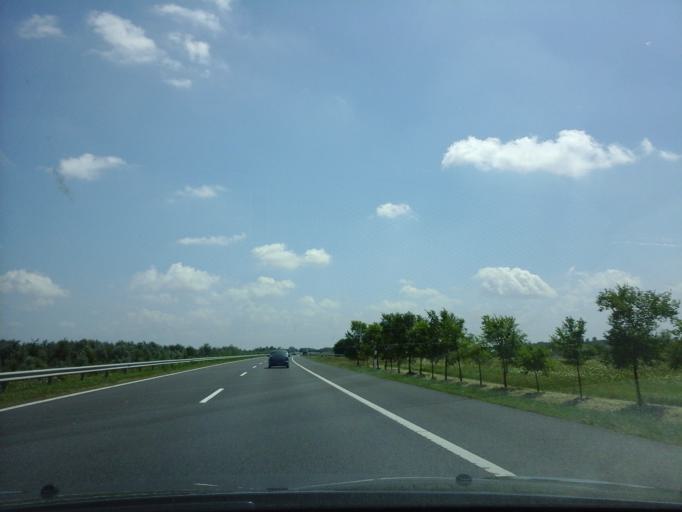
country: HU
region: Hajdu-Bihar
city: Gorbehaza
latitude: 47.7931
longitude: 21.2503
